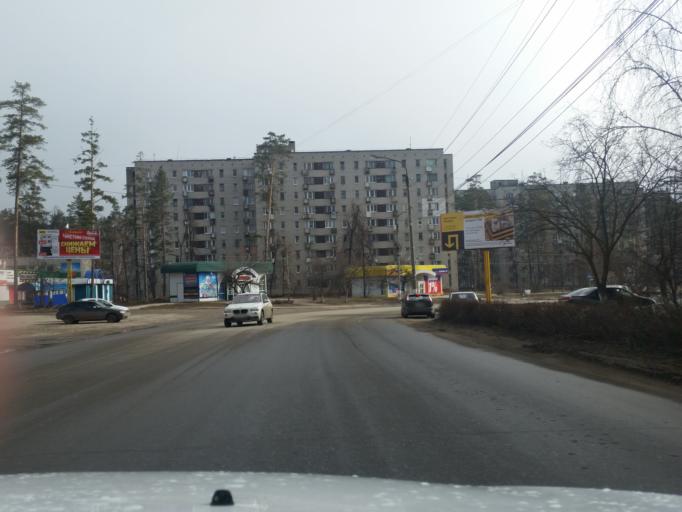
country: RU
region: Ulyanovsk
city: Dimitrovgrad
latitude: 54.2375
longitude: 49.5639
